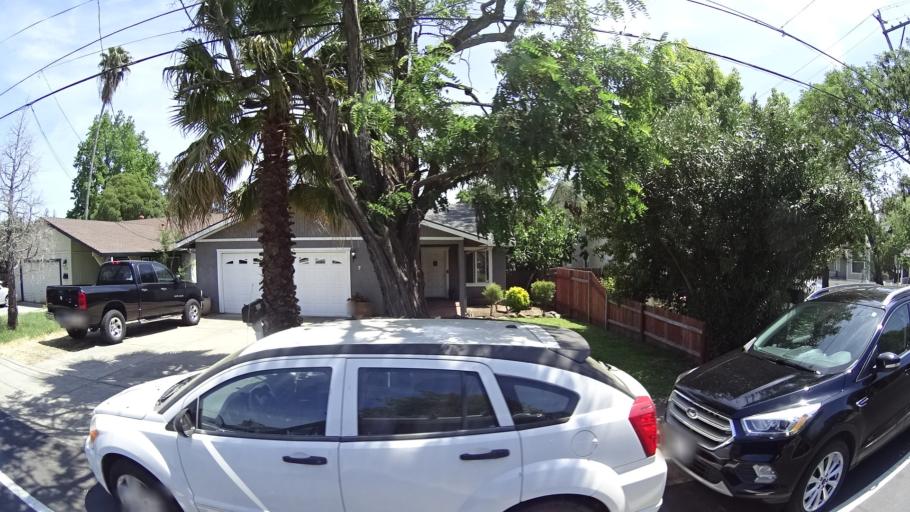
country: US
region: California
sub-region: Placer County
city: Rocklin
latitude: 38.7932
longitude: -121.2413
